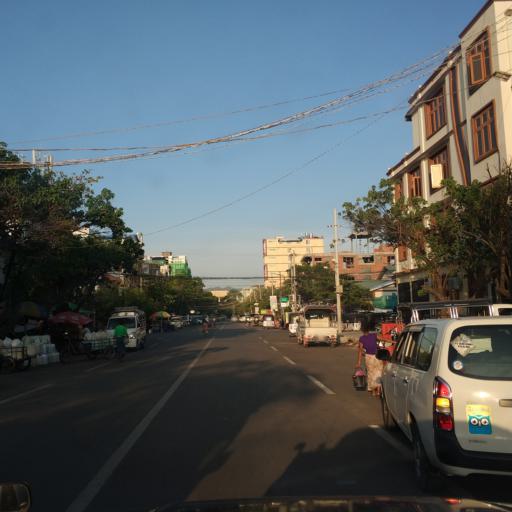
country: MM
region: Mandalay
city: Mandalay
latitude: 21.9750
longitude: 96.0912
